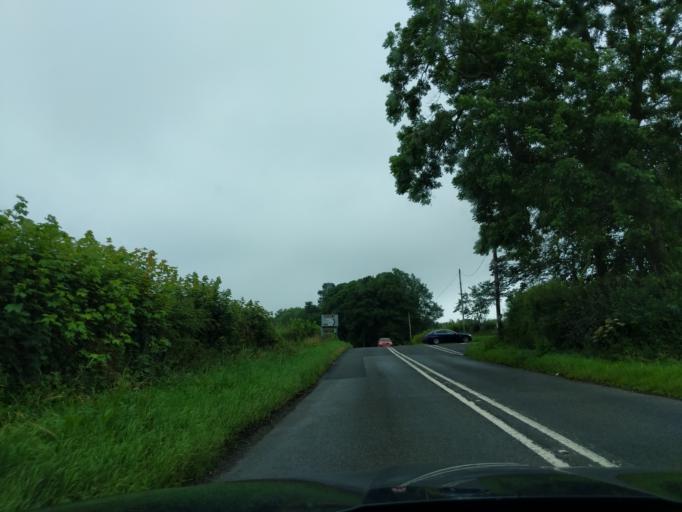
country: GB
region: England
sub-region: Northumberland
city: Lowick
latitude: 55.6492
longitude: -1.9990
